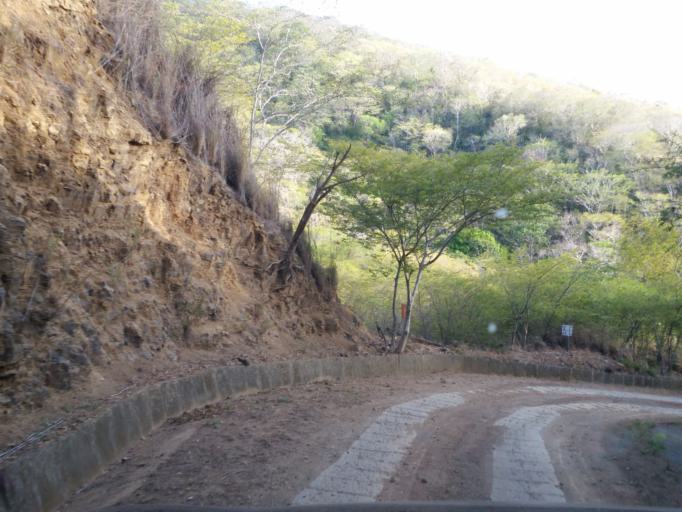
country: NI
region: Rivas
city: San Juan del Sur
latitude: 11.1808
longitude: -85.8115
